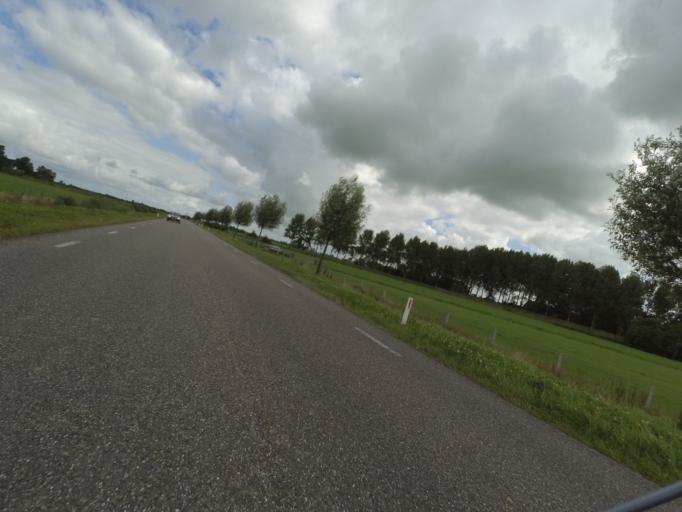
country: NL
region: Friesland
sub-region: Gemeente Kollumerland en Nieuwkruisland
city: Kollum
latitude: 53.2613
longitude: 6.1670
